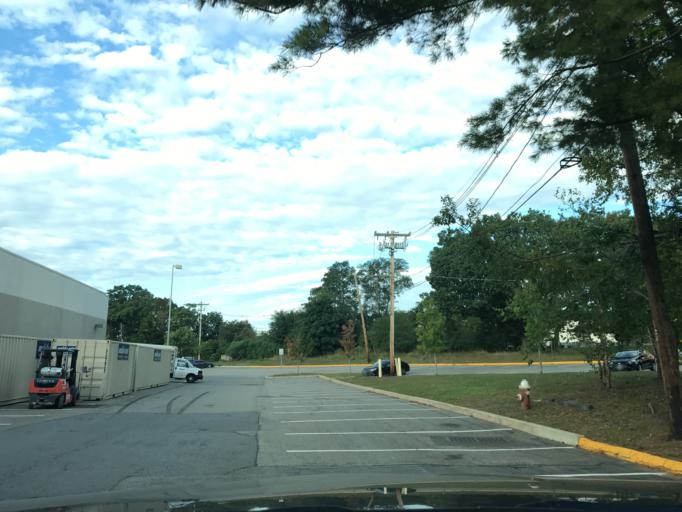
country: US
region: Massachusetts
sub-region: Middlesex County
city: Watertown
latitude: 42.3655
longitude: -71.1569
